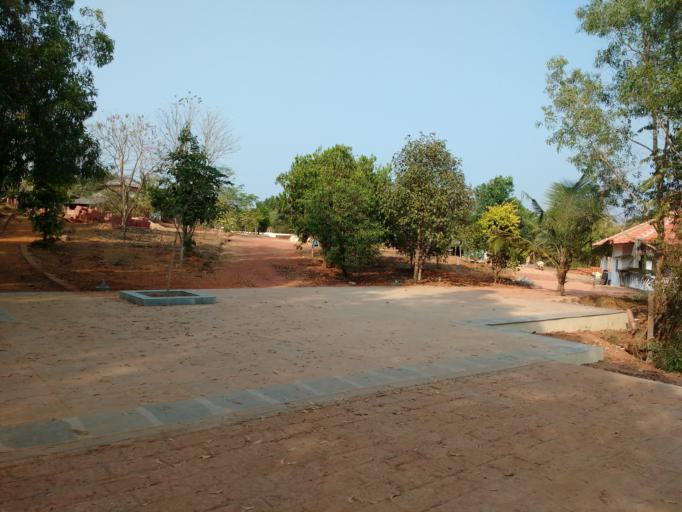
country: IN
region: Karnataka
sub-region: Dakshina Kannada
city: Mangalore
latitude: 12.9285
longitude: 74.9058
